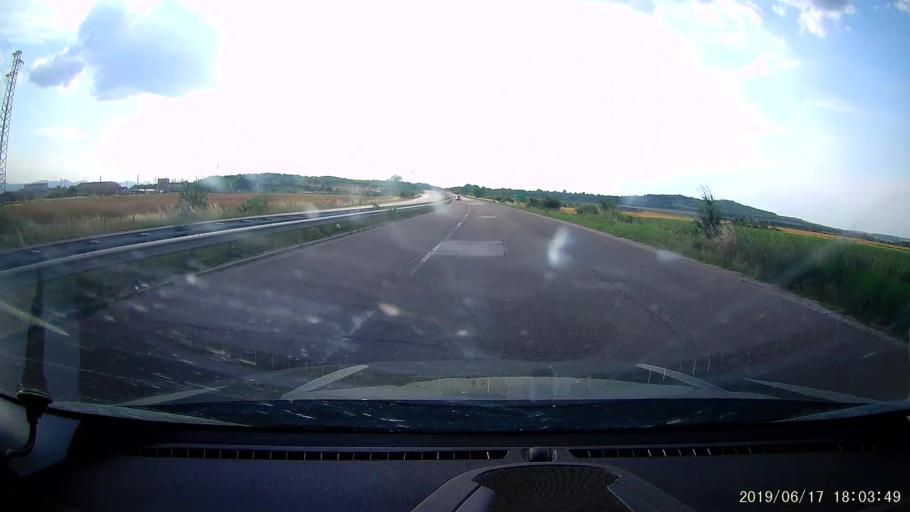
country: BG
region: Khaskovo
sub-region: Obshtina Svilengrad
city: Svilengrad
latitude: 41.7813
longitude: 26.2121
